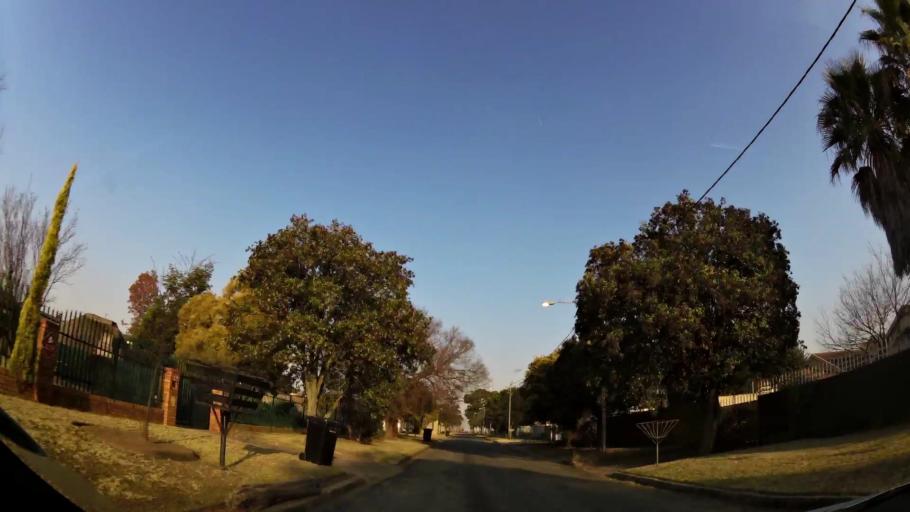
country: ZA
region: Gauteng
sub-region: Ekurhuleni Metropolitan Municipality
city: Springs
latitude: -26.3014
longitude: 28.4522
